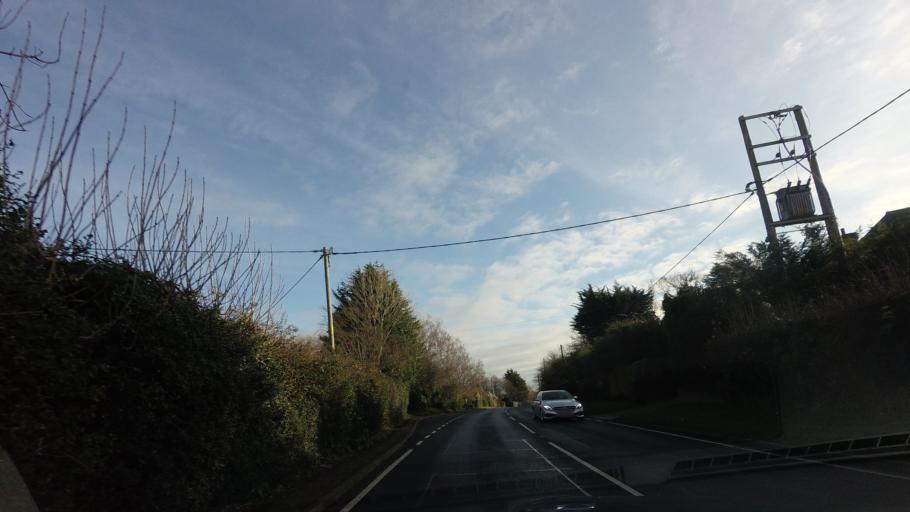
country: GB
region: England
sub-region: East Sussex
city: Bexhill-on-Sea
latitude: 50.8736
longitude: 0.4347
